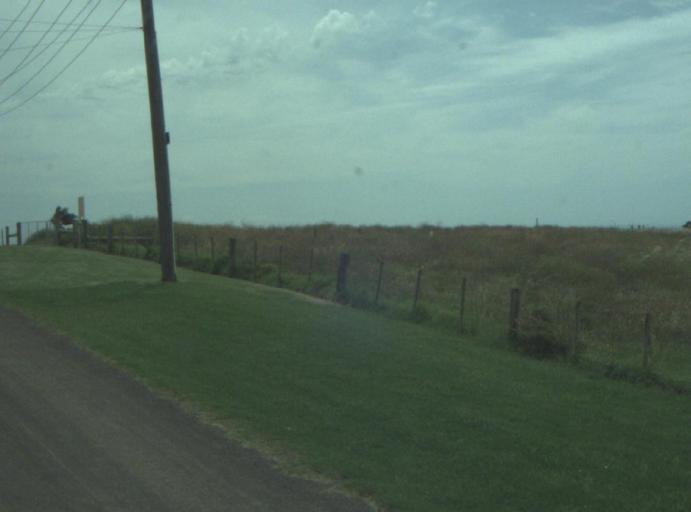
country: AU
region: Victoria
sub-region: Greater Geelong
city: Clifton Springs
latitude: -38.1231
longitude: 144.6455
